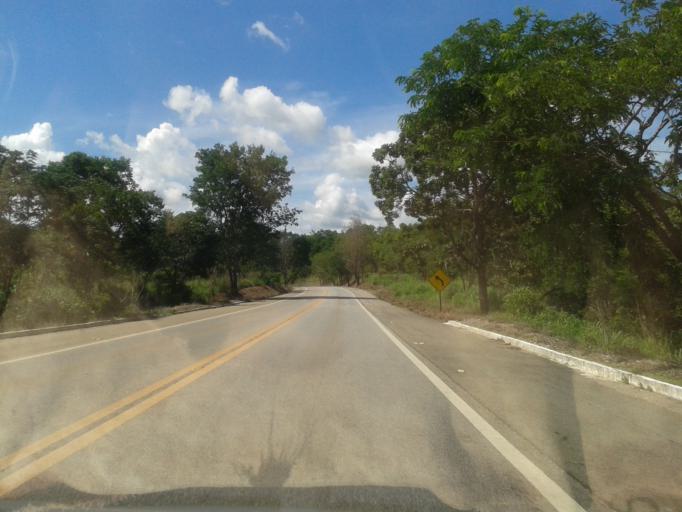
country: BR
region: Goias
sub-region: Goias
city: Goias
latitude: -15.6611
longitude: -50.2186
